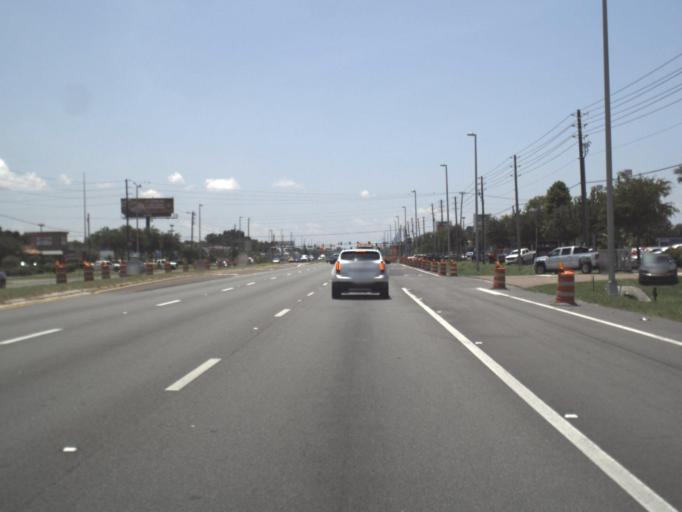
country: US
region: Florida
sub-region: Pasco County
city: Jasmine Estates
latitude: 28.3057
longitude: -82.7022
